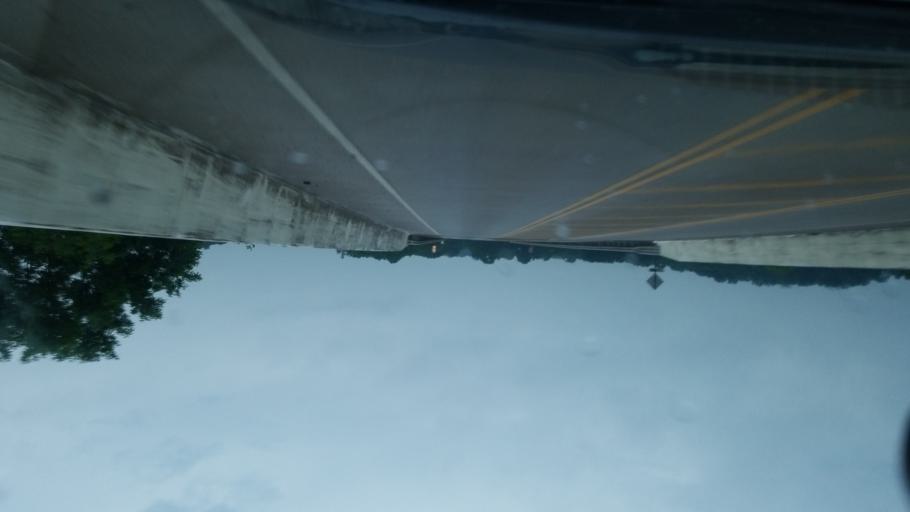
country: US
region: Ohio
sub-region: Fairfield County
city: Lancaster
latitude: 39.7723
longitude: -82.6880
